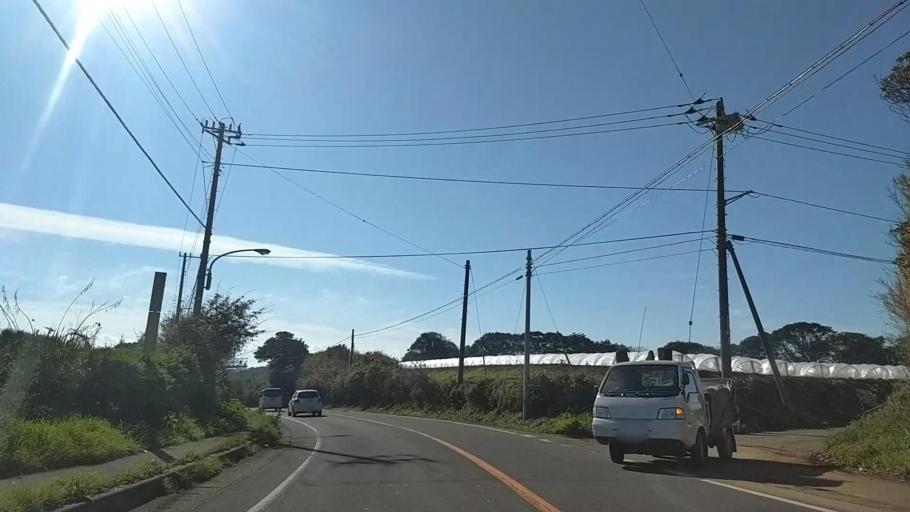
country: JP
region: Chiba
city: Asahi
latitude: 35.7066
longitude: 140.7407
